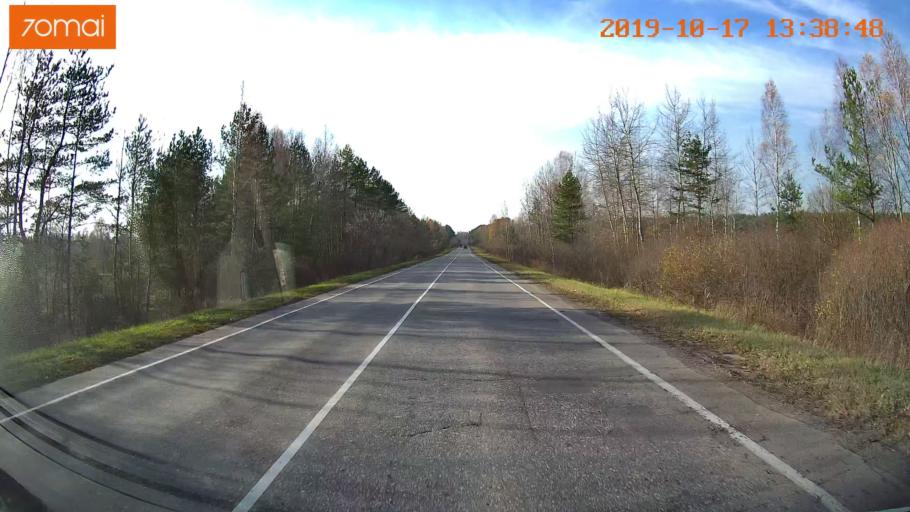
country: RU
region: Rjazan
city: Tuma
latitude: 55.1448
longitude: 40.6041
